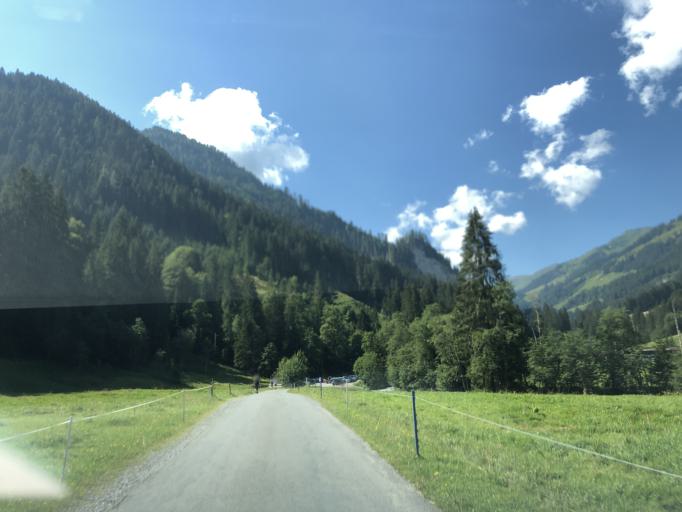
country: AT
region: Tyrol
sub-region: Politischer Bezirk Kitzbuhel
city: Kirchberg in Tirol
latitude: 47.3762
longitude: 12.3054
